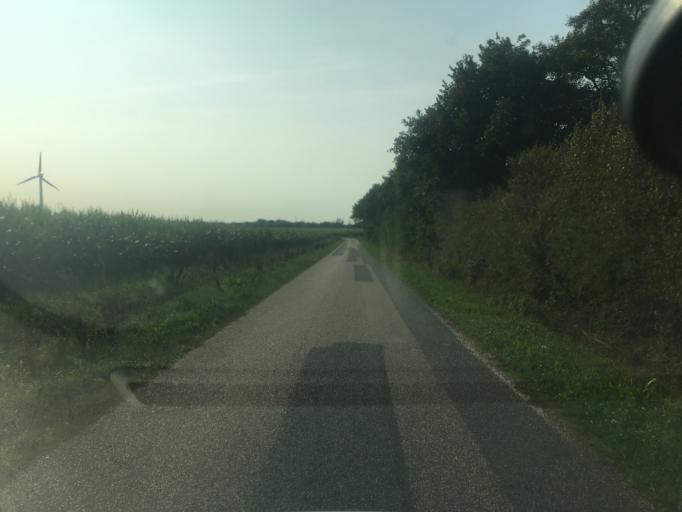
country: DK
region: South Denmark
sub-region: Tonder Kommune
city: Tonder
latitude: 54.9861
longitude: 8.9013
